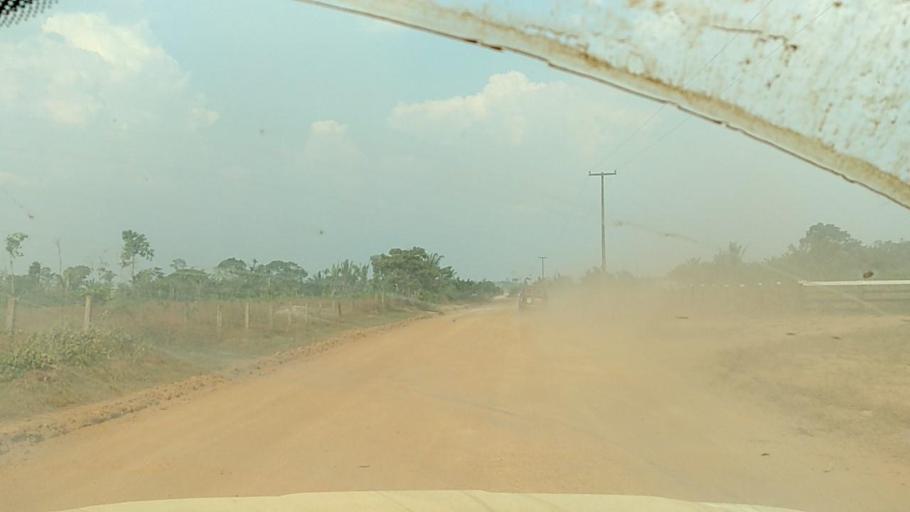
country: BR
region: Rondonia
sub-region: Porto Velho
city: Porto Velho
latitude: -8.6831
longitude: -63.1981
